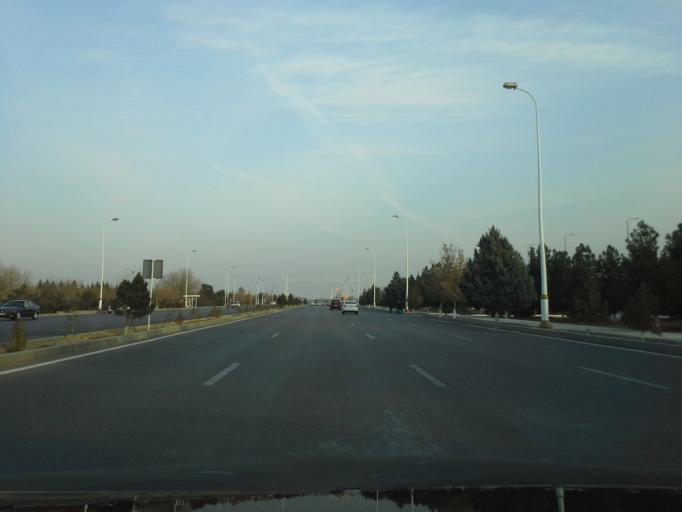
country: TM
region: Ahal
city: Abadan
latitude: 38.0354
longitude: 58.2210
